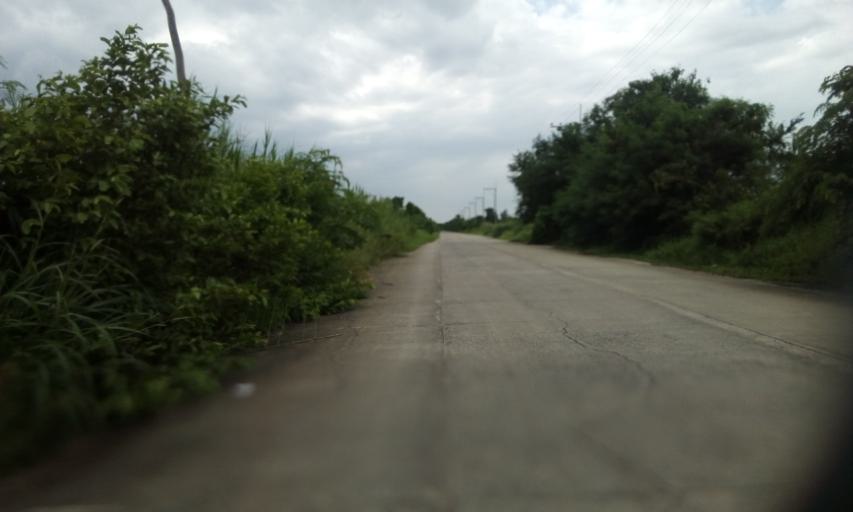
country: TH
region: Pathum Thani
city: Nong Suea
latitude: 14.0617
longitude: 100.8354
